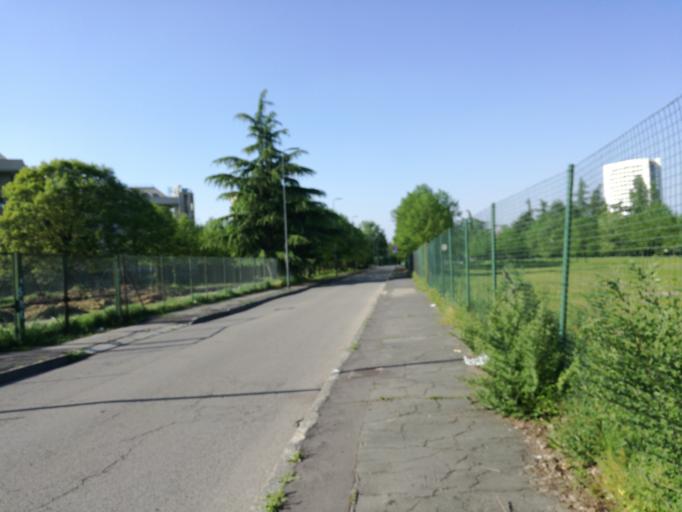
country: IT
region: Lombardy
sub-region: Citta metropolitana di Milano
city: Milano
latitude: 45.4326
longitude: 9.1907
